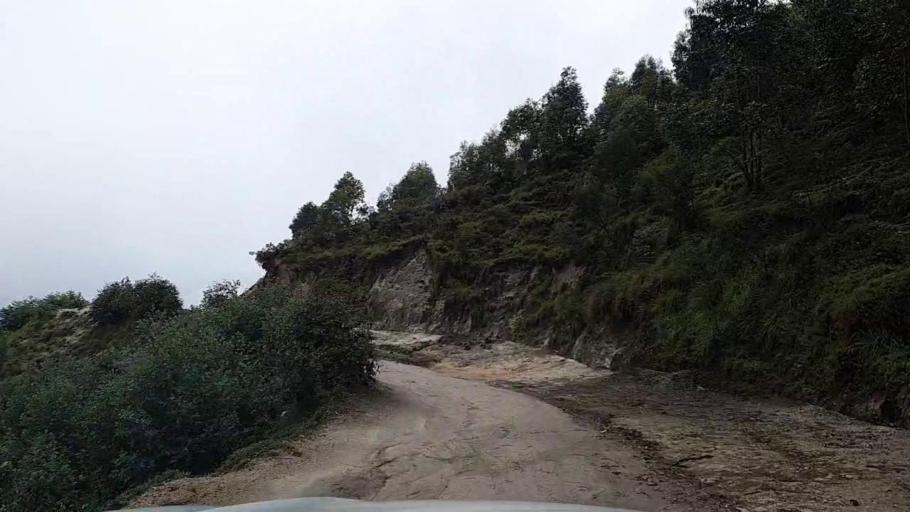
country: RW
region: Southern Province
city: Gikongoro
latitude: -2.3690
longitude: 29.4975
